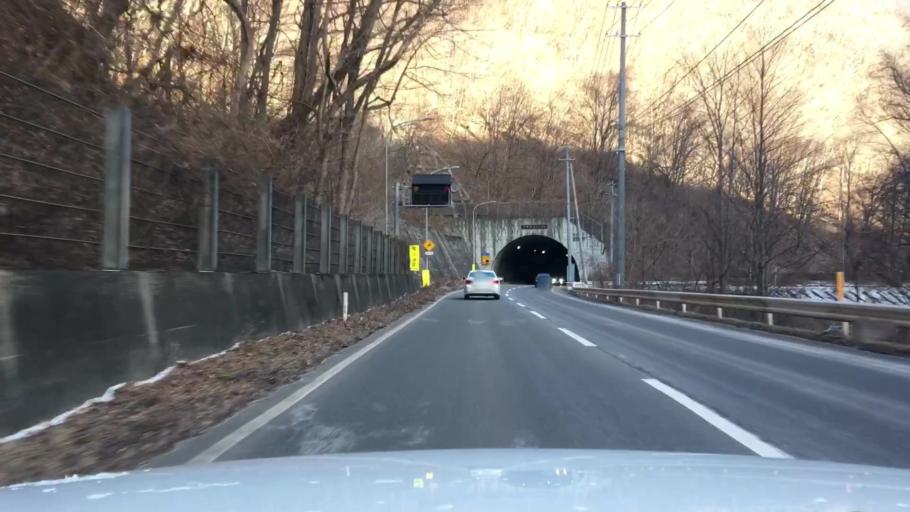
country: JP
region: Iwate
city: Tono
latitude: 39.6397
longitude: 141.5368
